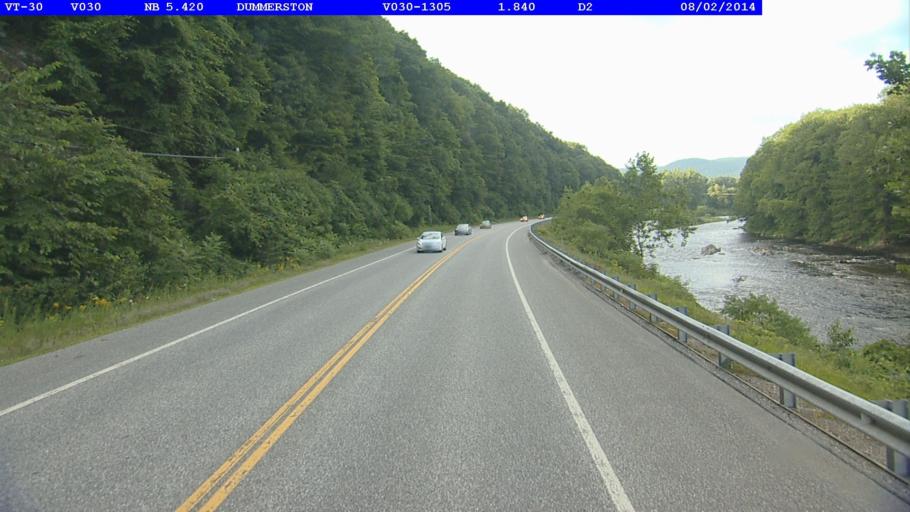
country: US
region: Vermont
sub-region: Windham County
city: West Brattleboro
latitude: 42.9199
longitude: -72.6154
